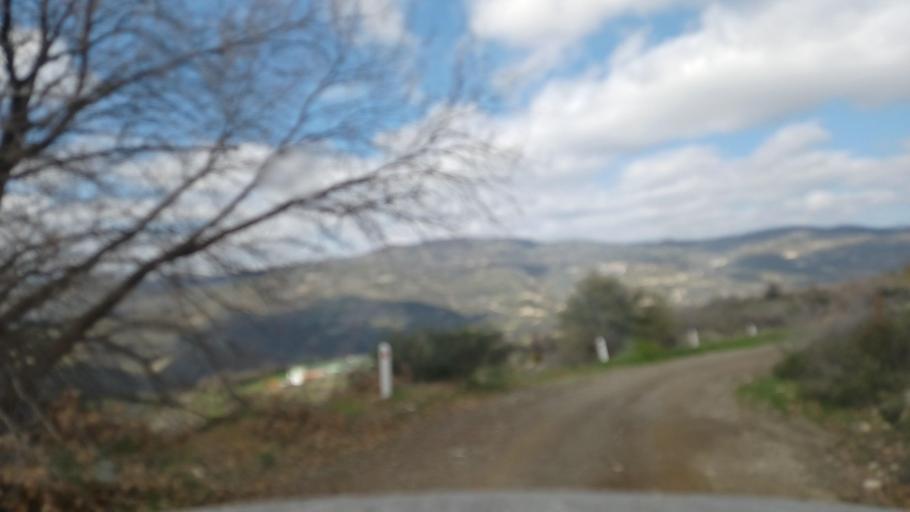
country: CY
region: Limassol
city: Pachna
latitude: 34.8424
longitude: 32.7354
